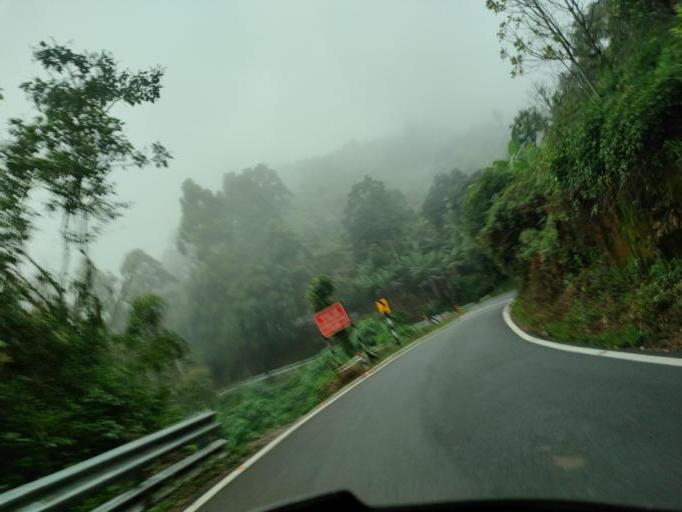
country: IN
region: Tamil Nadu
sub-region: Dindigul
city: Ayakudi
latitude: 10.3340
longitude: 77.5623
